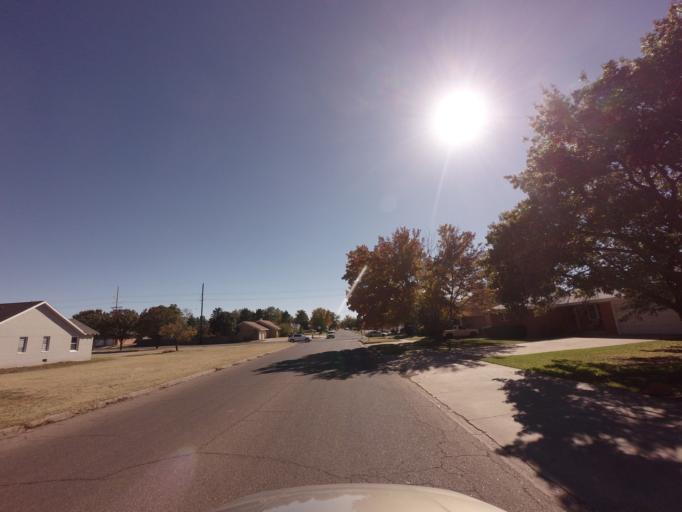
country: US
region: New Mexico
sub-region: Curry County
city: Clovis
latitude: 34.4199
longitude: -103.2028
